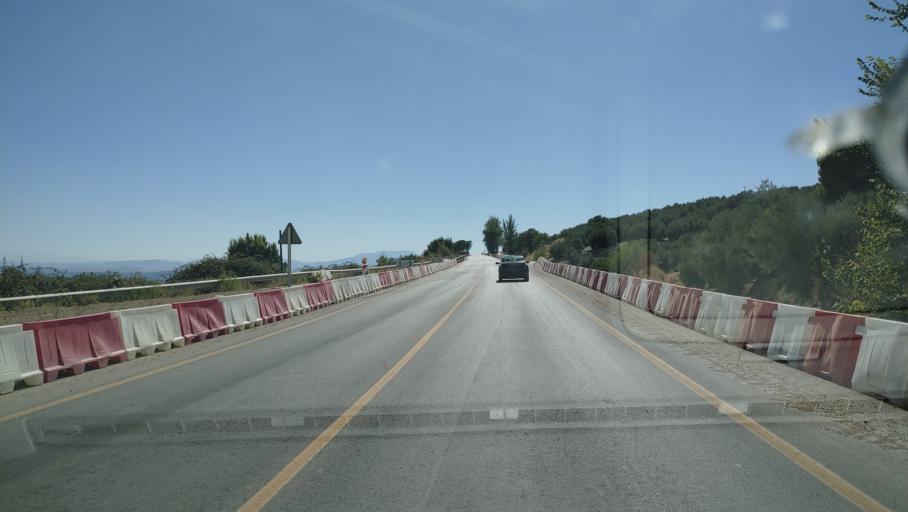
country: ES
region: Andalusia
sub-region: Provincia de Jaen
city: Iznatoraf
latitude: 38.1468
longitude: -3.0251
